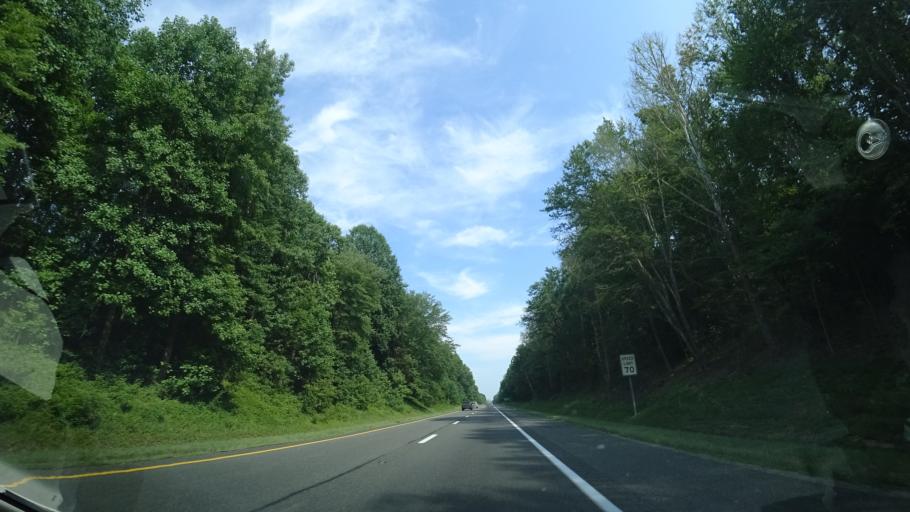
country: US
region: Virginia
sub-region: Goochland County
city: Goochland
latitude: 37.8362
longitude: -77.9732
